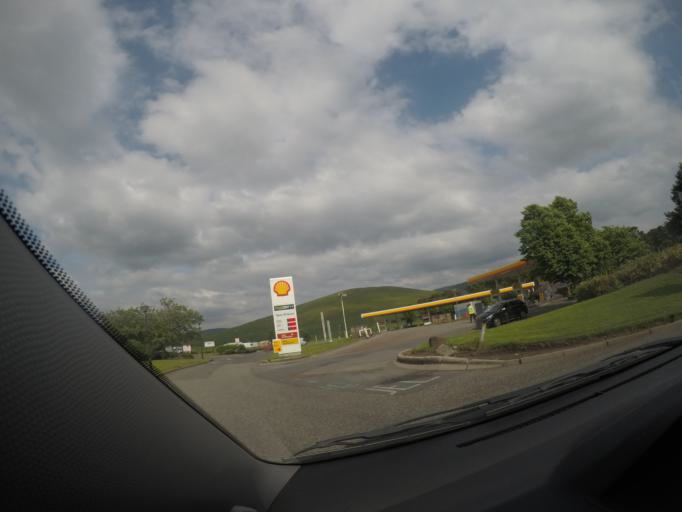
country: GB
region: Scotland
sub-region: South Lanarkshire
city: Douglas
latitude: 55.5067
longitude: -3.6955
